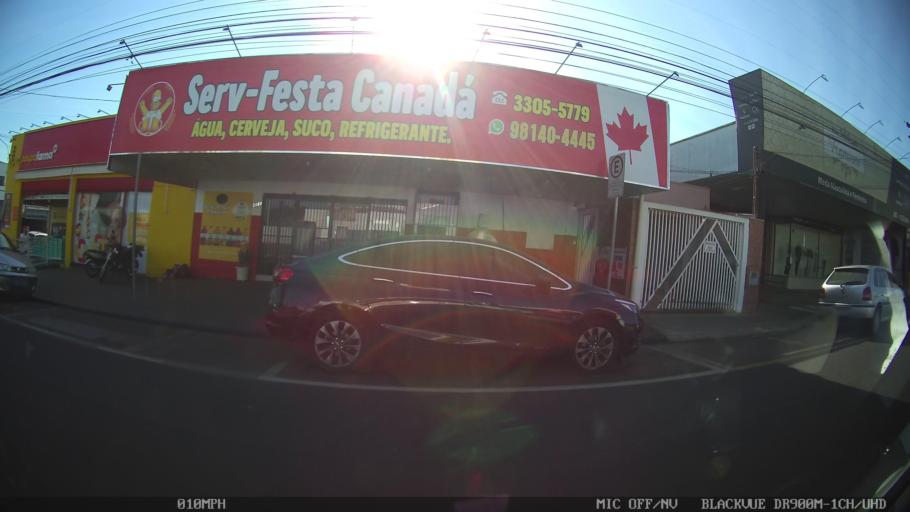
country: BR
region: Sao Paulo
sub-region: Sao Jose Do Rio Preto
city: Sao Jose do Rio Preto
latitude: -20.7978
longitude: -49.3668
